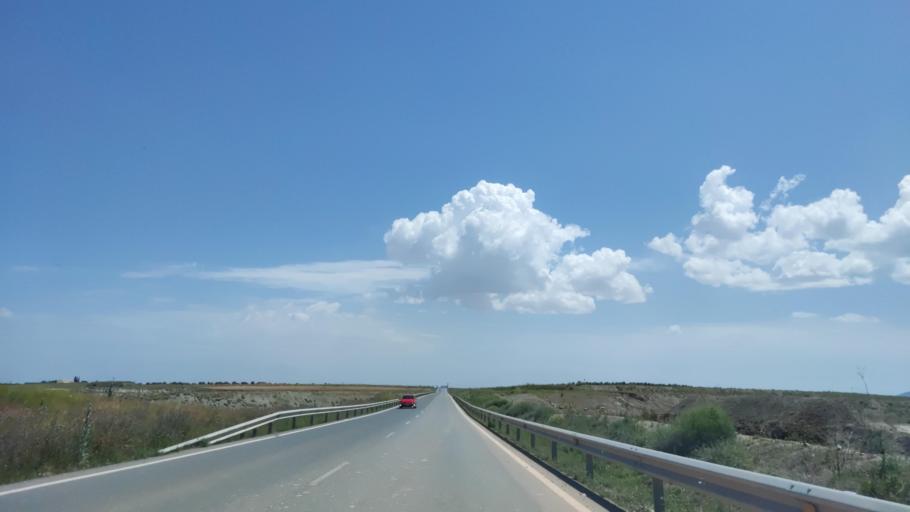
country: ES
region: Castille-La Mancha
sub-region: Province of Toledo
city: Mascaraque
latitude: 39.7144
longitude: -3.8288
